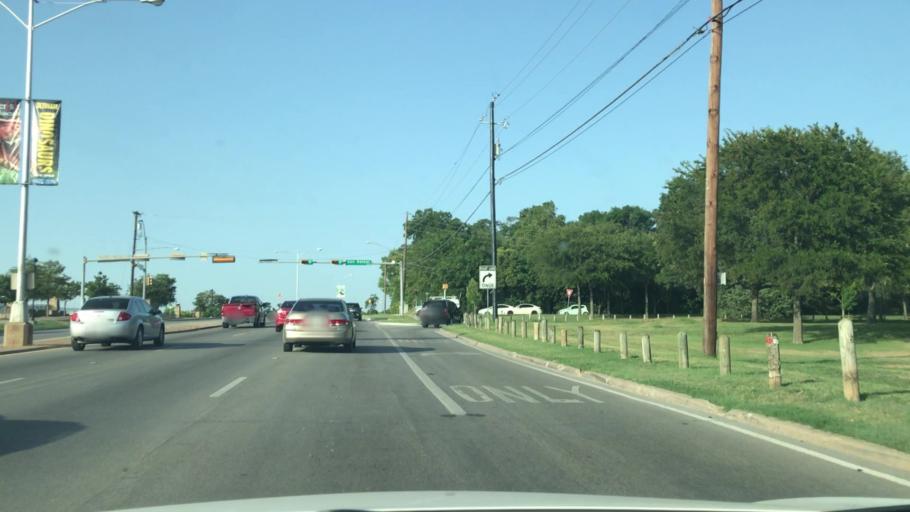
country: US
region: Texas
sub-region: Dallas County
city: Highland Park
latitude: 32.8139
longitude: -96.7250
